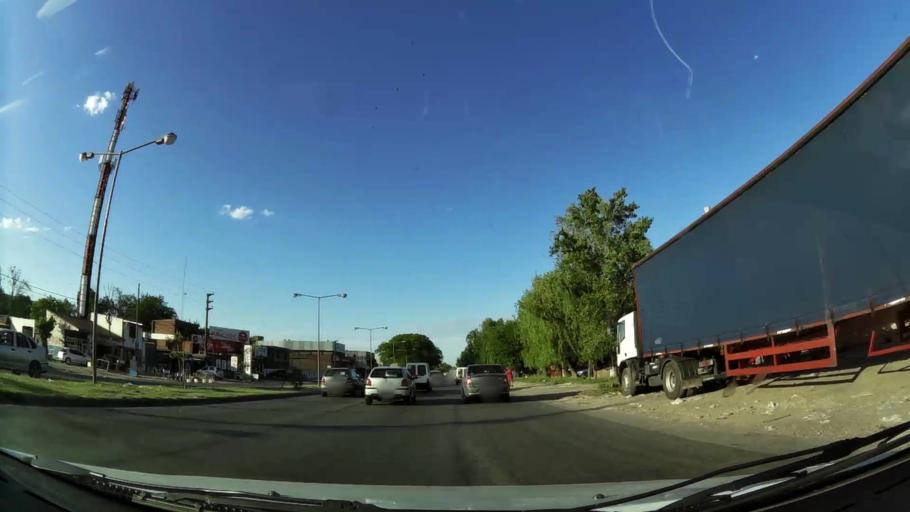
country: AR
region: Buenos Aires
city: Caseros
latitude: -34.5577
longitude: -58.5863
